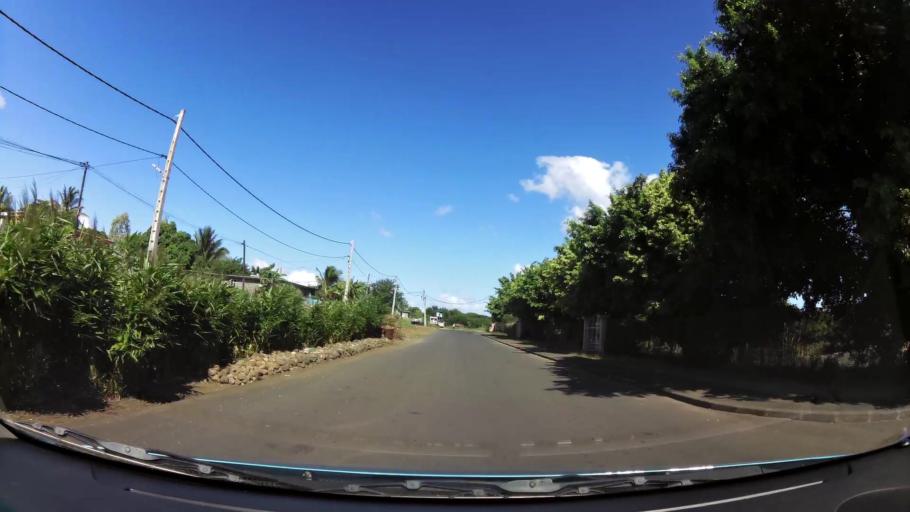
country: MU
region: Black River
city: Cascavelle
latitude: -20.2624
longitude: 57.4104
